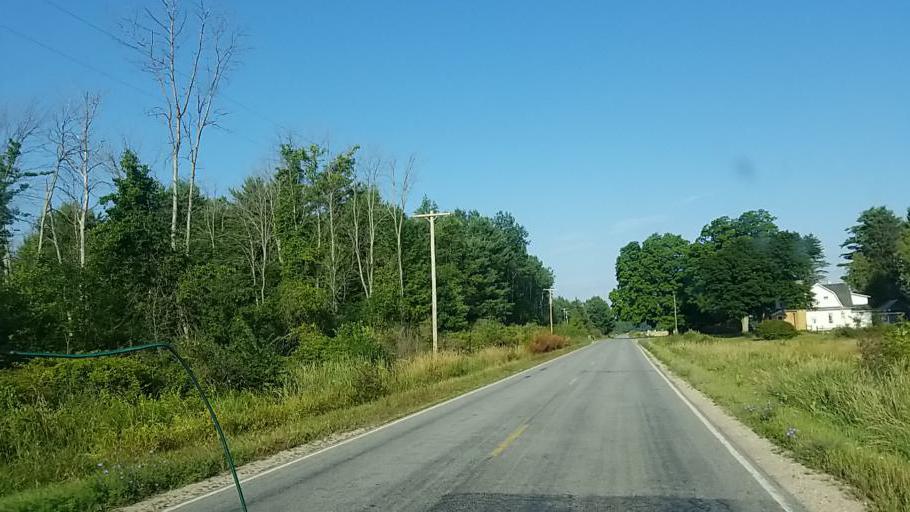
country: US
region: Michigan
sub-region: Newaygo County
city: Newaygo
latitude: 43.3508
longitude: -85.8902
